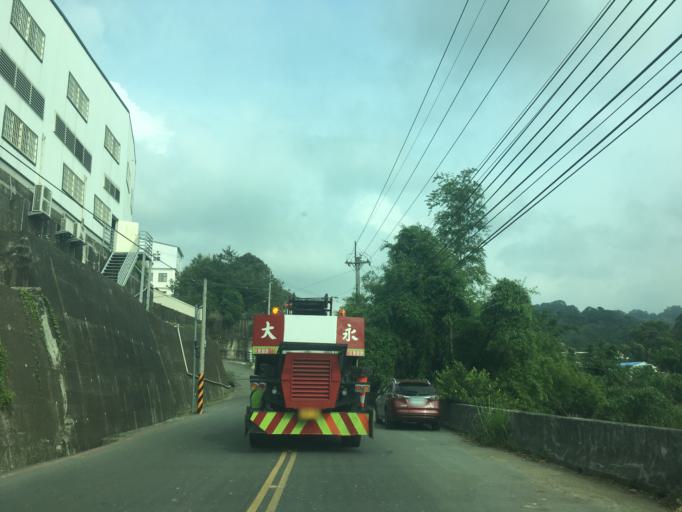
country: TW
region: Taiwan
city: Fengyuan
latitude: 24.2368
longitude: 120.7412
